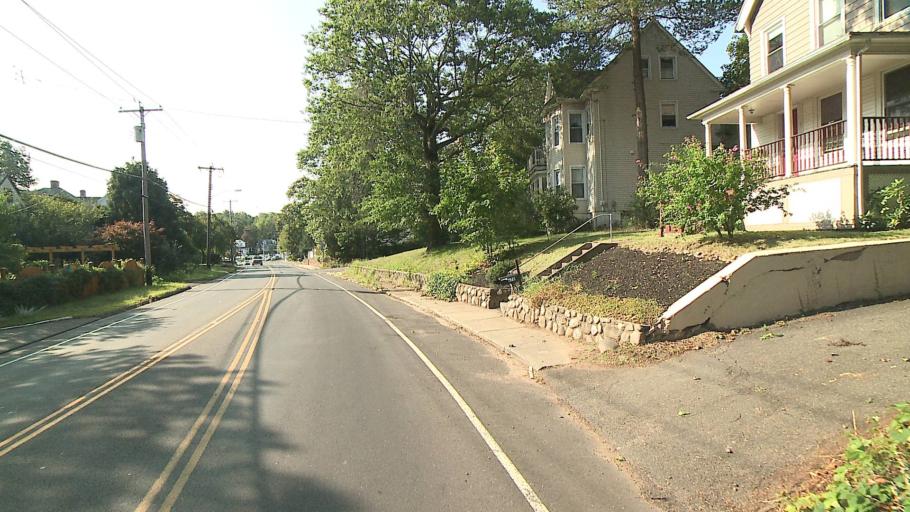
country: US
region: Connecticut
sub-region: New Haven County
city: New Haven
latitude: 41.3091
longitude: -72.9702
